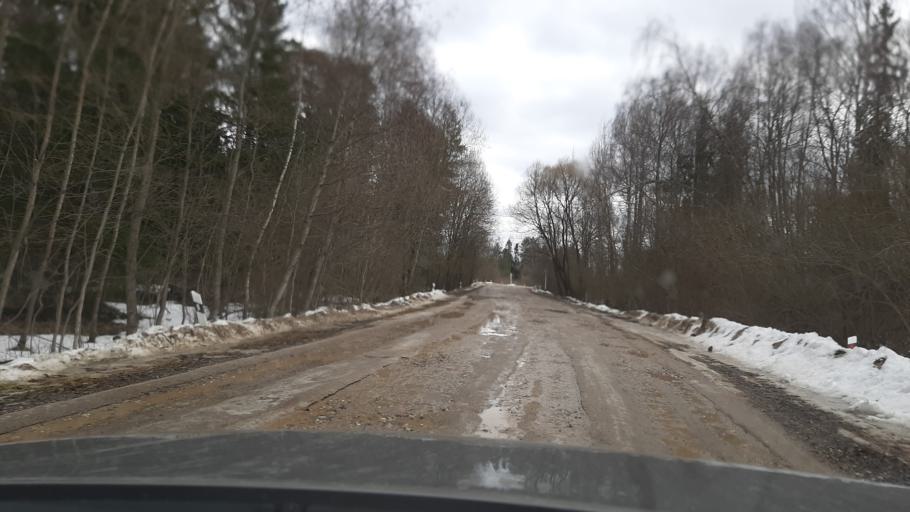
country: RU
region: Ivanovo
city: Teykovo
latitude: 56.8853
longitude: 40.6194
